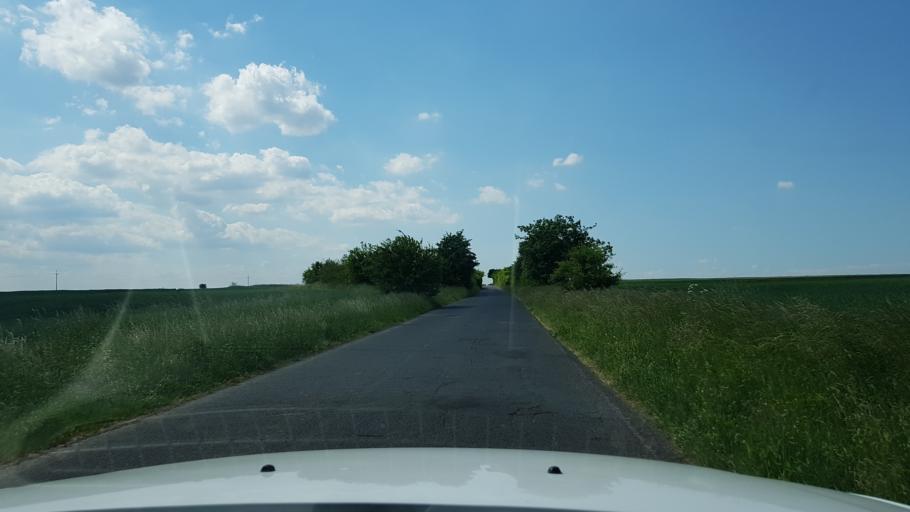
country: PL
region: West Pomeranian Voivodeship
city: Trzcinsko Zdroj
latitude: 52.9903
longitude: 14.5966
